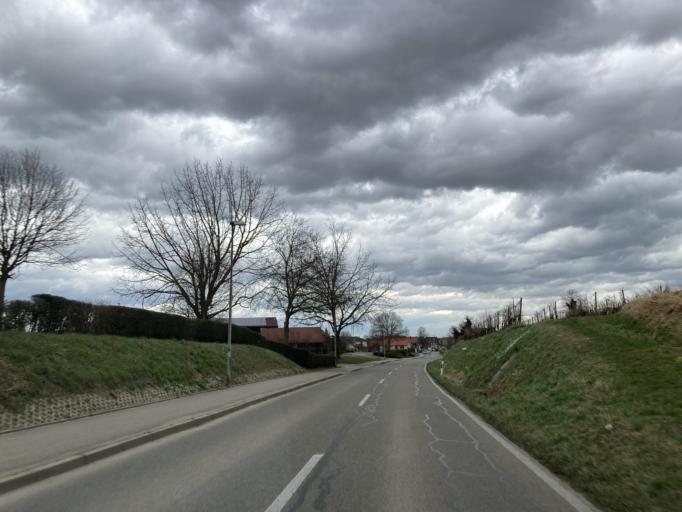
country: DE
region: Baden-Wuerttemberg
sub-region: Freiburg Region
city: Vogtsburg
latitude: 48.1280
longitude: 7.6531
